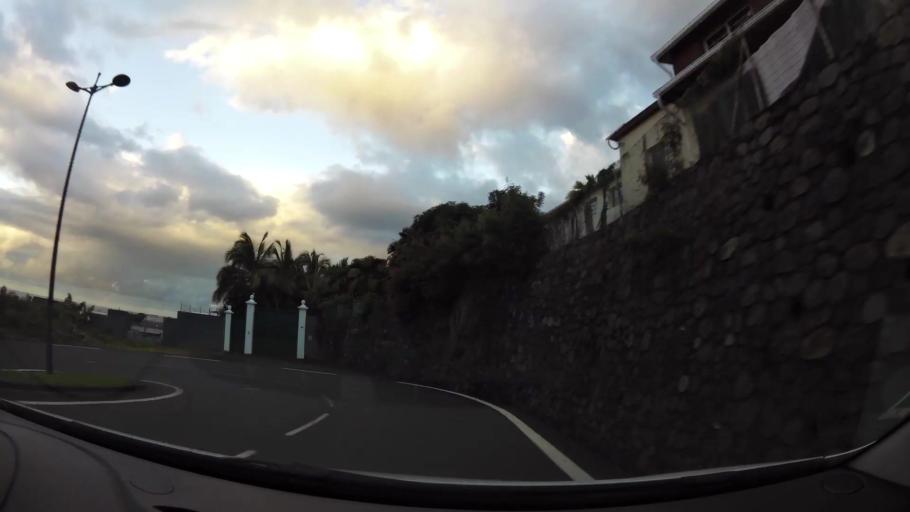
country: RE
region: Reunion
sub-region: Reunion
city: Saint-Denis
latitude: -20.9047
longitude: 55.4642
